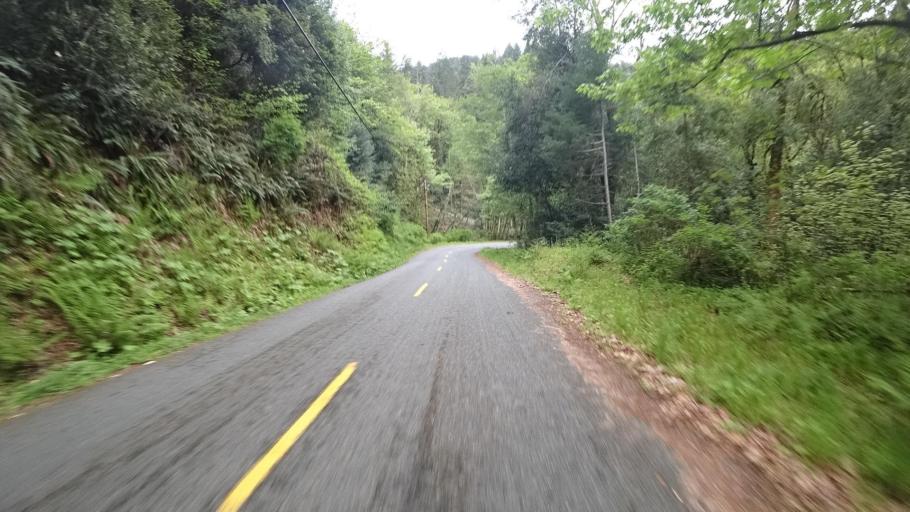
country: US
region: California
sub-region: Humboldt County
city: Blue Lake
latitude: 40.9466
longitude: -123.8445
